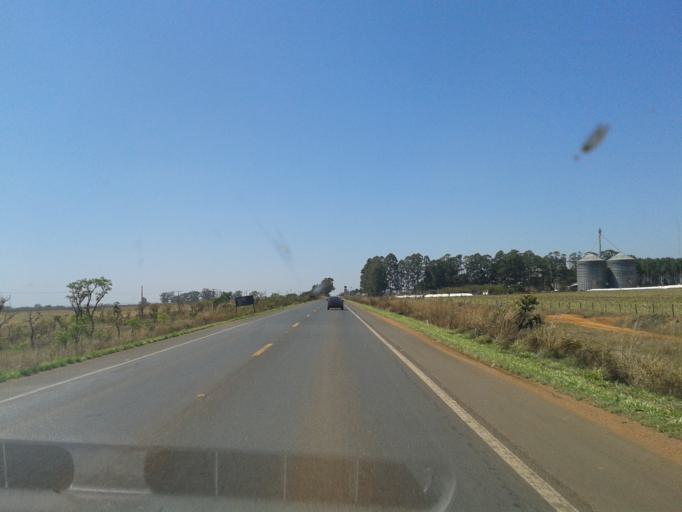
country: BR
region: Minas Gerais
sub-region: Uberaba
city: Uberaba
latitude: -19.3100
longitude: -47.5777
